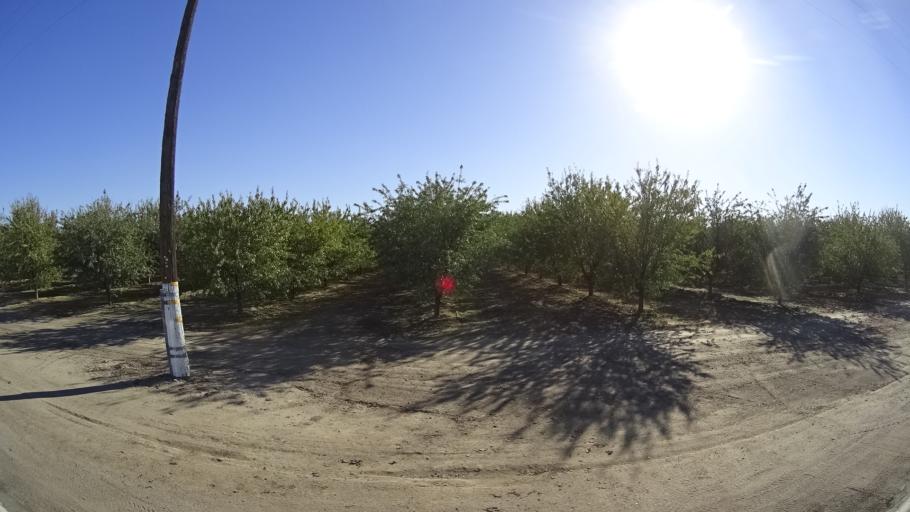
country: US
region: California
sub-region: Kern County
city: Greenacres
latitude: 35.2813
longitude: -119.1274
